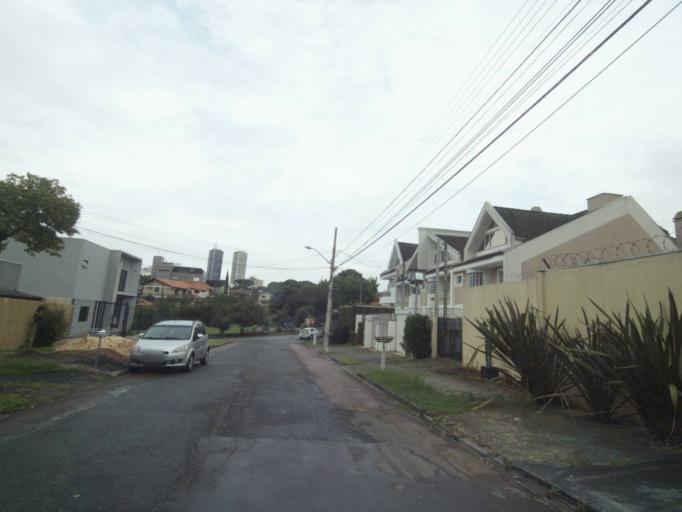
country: BR
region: Parana
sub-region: Curitiba
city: Curitiba
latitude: -25.4170
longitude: -49.2851
